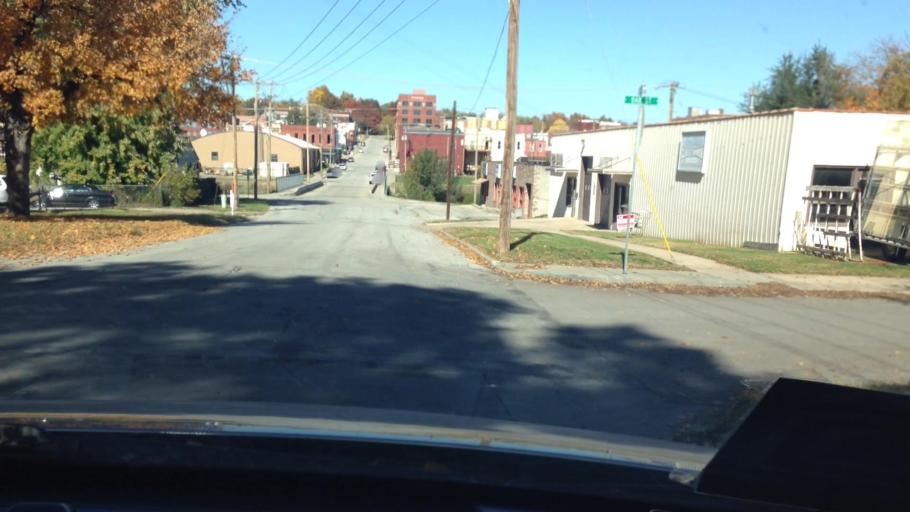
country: US
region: Kansas
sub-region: Leavenworth County
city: Leavenworth
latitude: 39.3145
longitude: -94.9160
